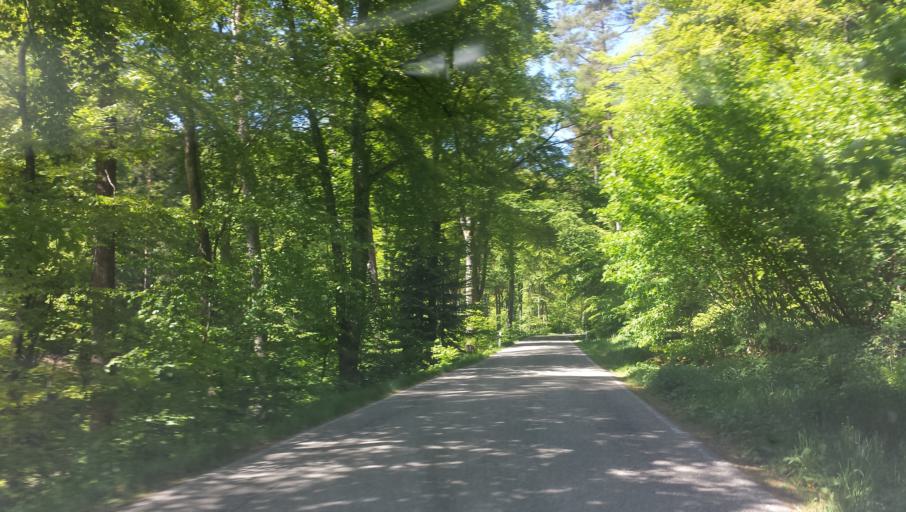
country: DE
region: Rheinland-Pfalz
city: Ramberg
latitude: 49.2856
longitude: 8.0158
